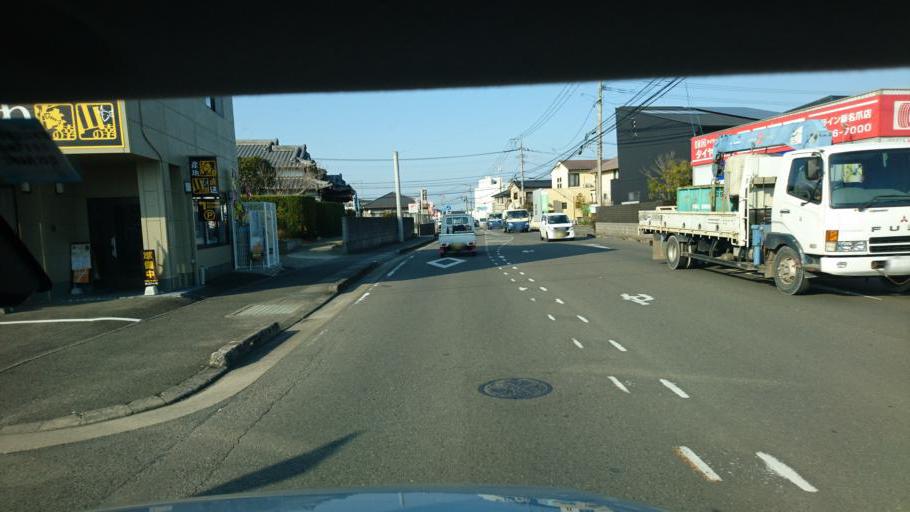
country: JP
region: Miyazaki
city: Miyazaki-shi
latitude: 31.9759
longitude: 131.4403
